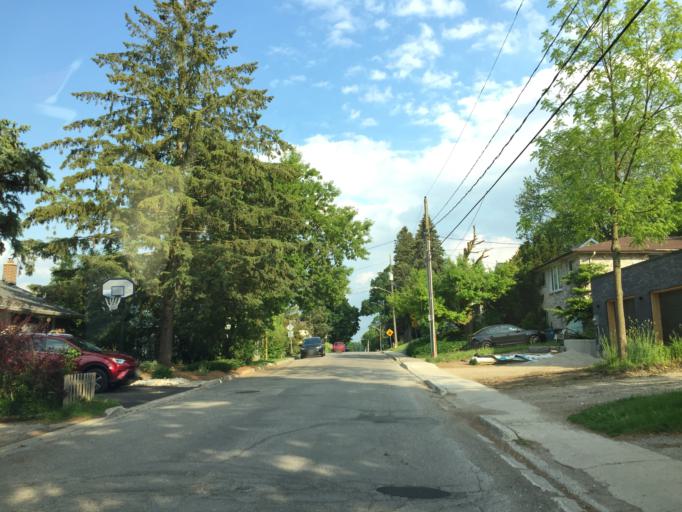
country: CA
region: Ontario
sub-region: Wellington County
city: Guelph
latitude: 43.5529
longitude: -80.2689
